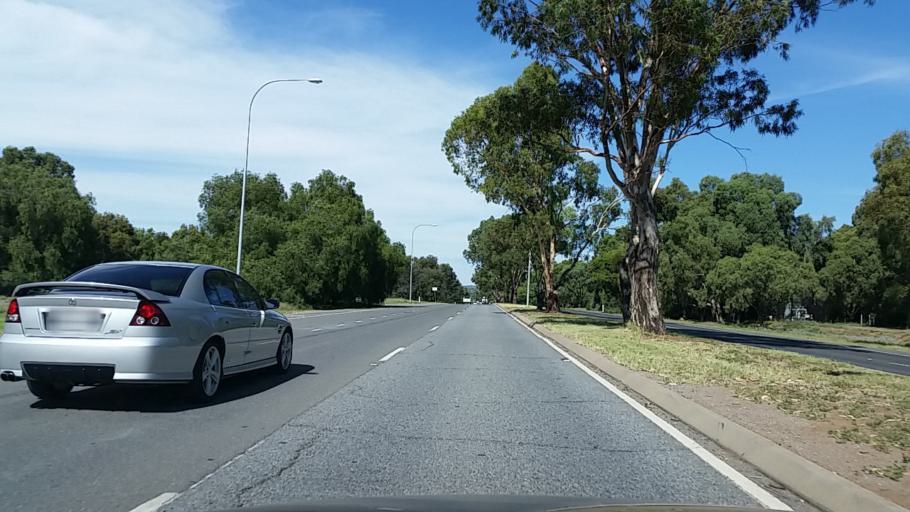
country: AU
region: South Australia
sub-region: Salisbury
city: Ingle Farm
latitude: -34.8258
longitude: 138.6078
